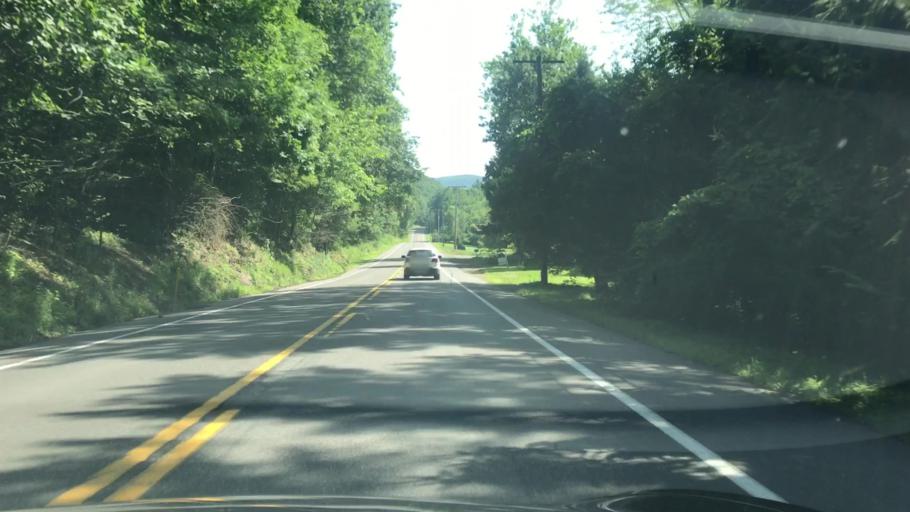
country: US
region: Pennsylvania
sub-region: Lycoming County
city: Garden View
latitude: 41.4317
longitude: -77.0062
